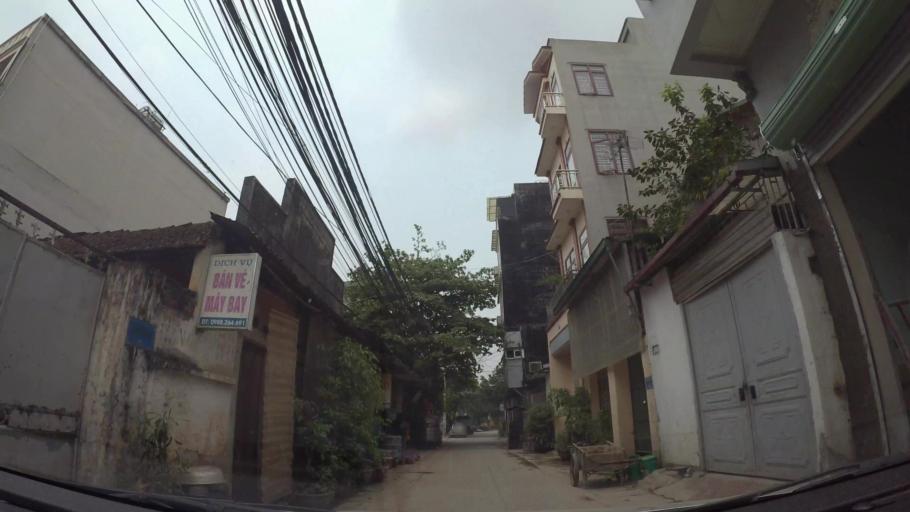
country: VN
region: Ha Noi
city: Ha Dong
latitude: 20.9835
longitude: 105.7489
